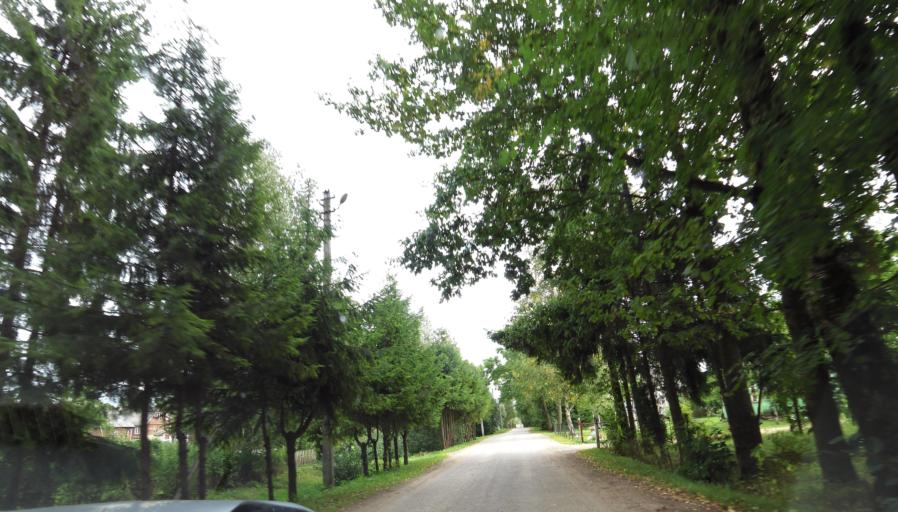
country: LT
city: Linkuva
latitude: 56.0602
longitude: 24.1474
